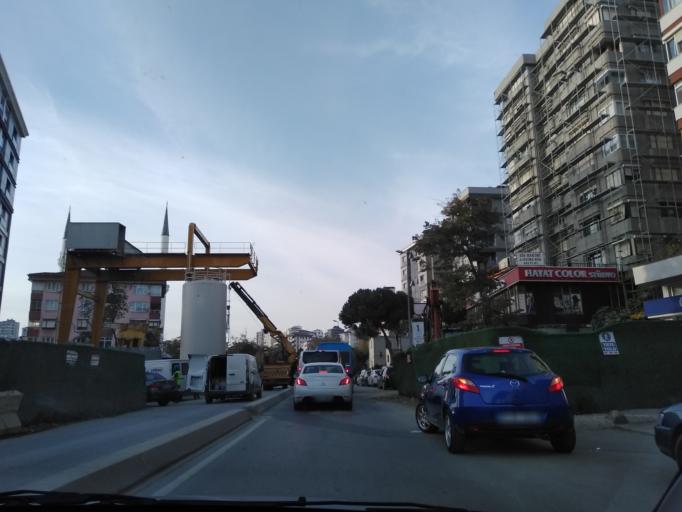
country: TR
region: Istanbul
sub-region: Atasehir
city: Atasehir
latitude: 40.9600
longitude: 29.0944
